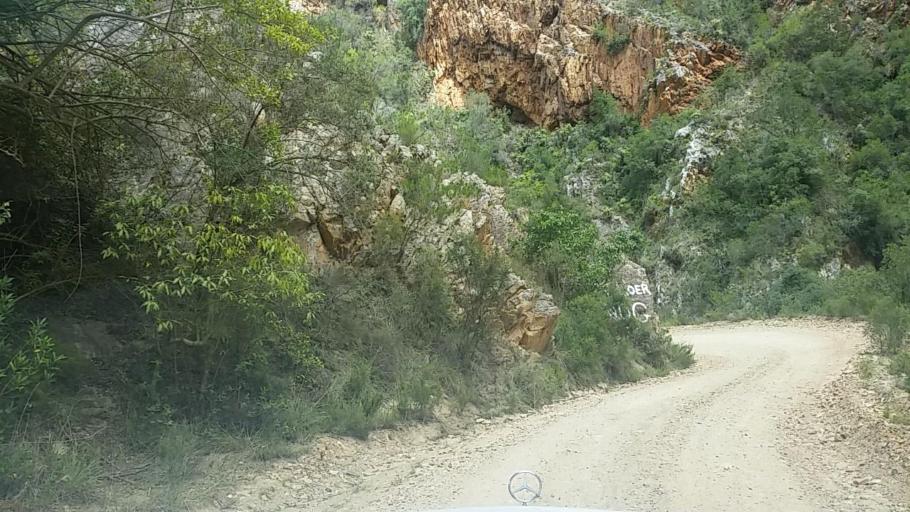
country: ZA
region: Western Cape
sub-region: Eden District Municipality
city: Knysna
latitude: -33.8028
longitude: 23.1805
